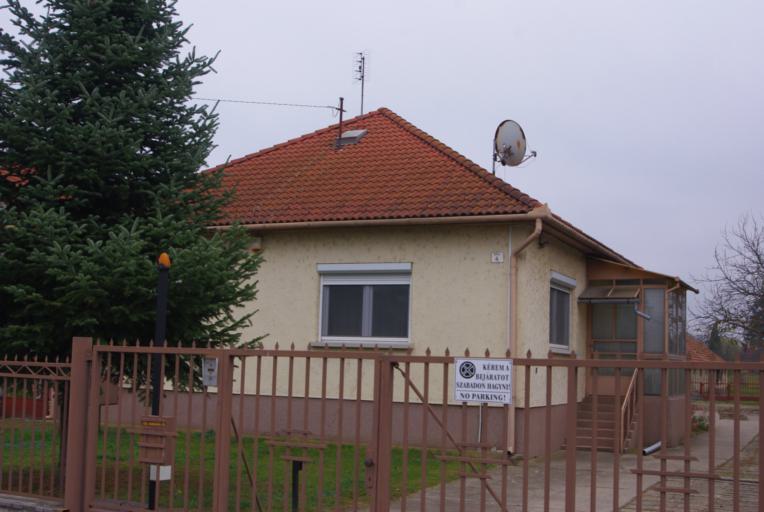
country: HU
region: Pest
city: Isaszeg
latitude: 47.5337
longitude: 19.3915
